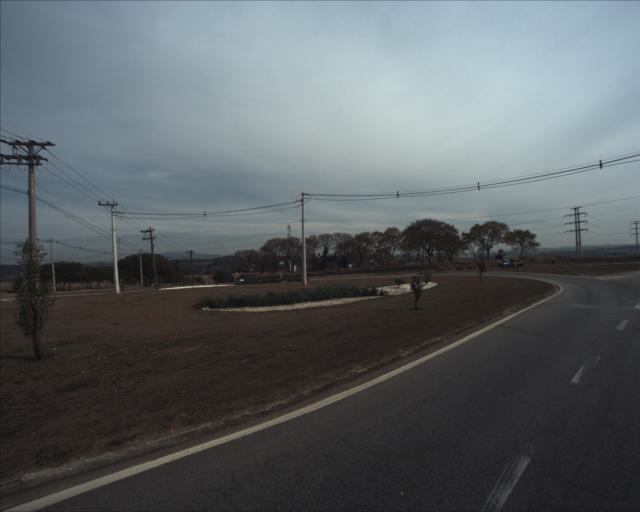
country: BR
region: Sao Paulo
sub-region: Sorocaba
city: Sorocaba
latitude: -23.4503
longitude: -47.5134
